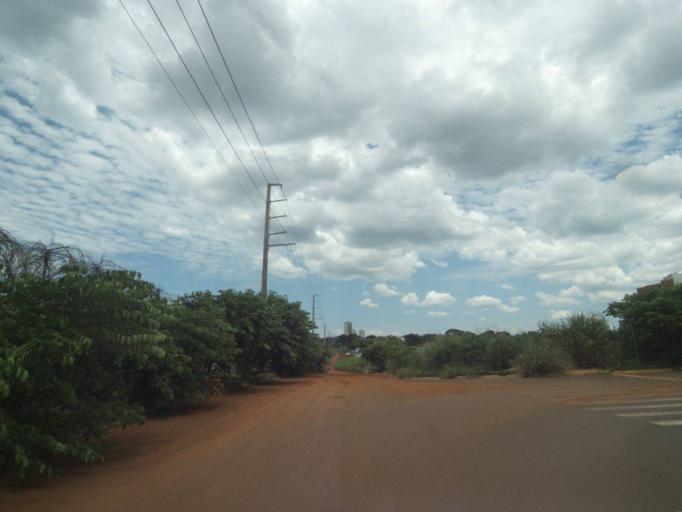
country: BR
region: Parana
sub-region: Londrina
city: Londrina
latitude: -23.3232
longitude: -51.1882
